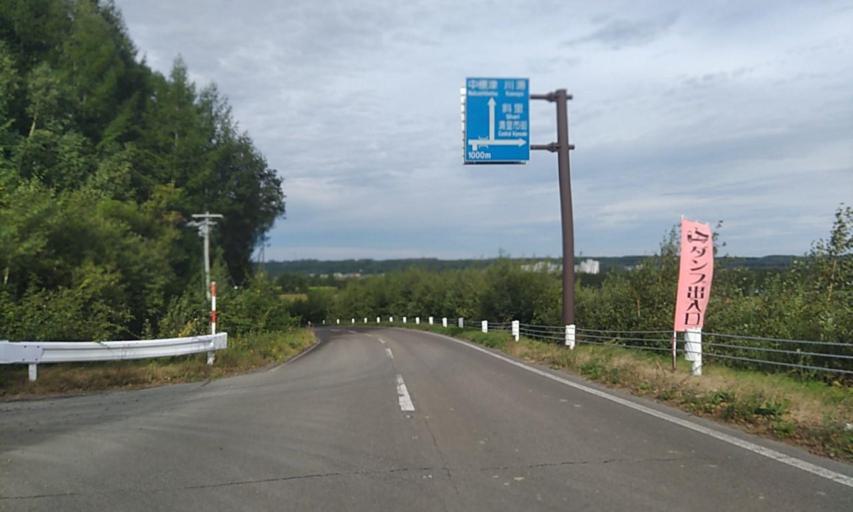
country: JP
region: Hokkaido
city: Abashiri
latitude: 43.7955
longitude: 144.5676
